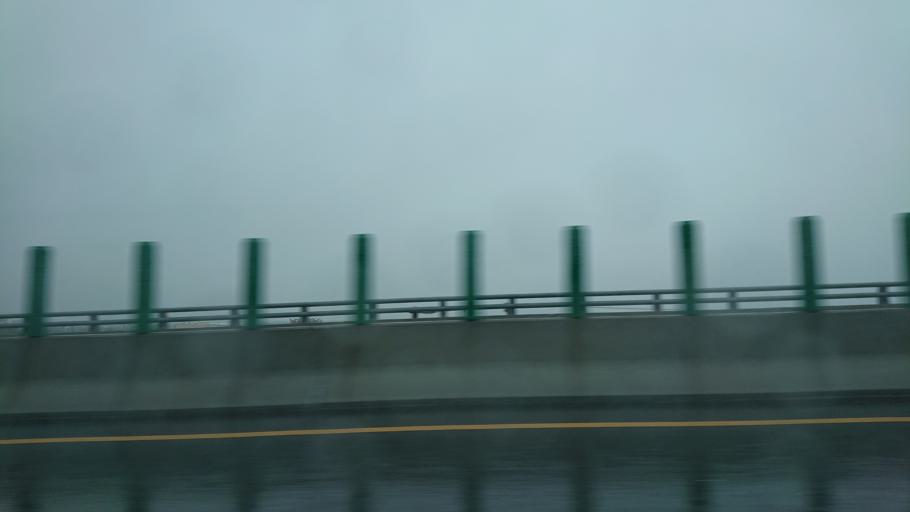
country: TW
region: Taiwan
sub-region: Changhua
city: Chang-hua
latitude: 23.9488
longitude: 120.3280
